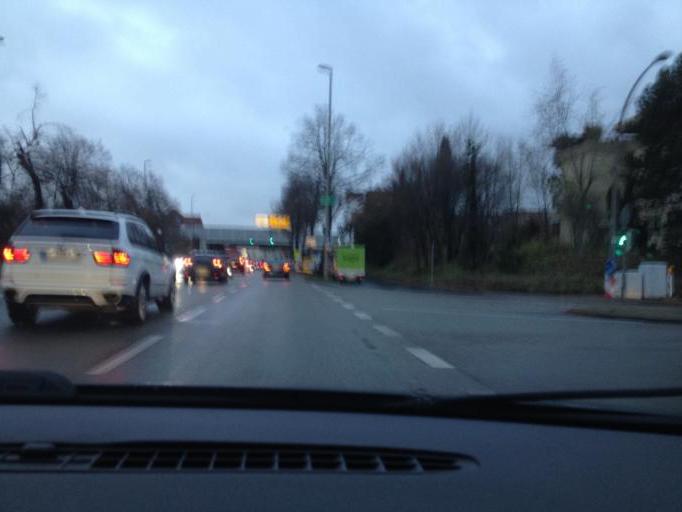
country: DE
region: Baden-Wuerttemberg
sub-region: Regierungsbezirk Stuttgart
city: Ludwigsburg
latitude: 48.9041
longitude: 9.1787
